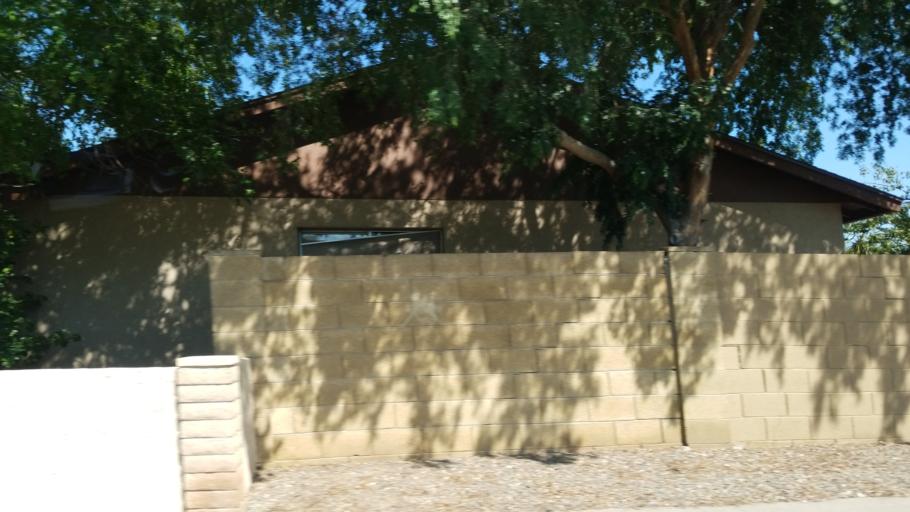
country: US
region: Arizona
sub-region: Maricopa County
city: Glendale
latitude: 33.5567
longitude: -112.1732
